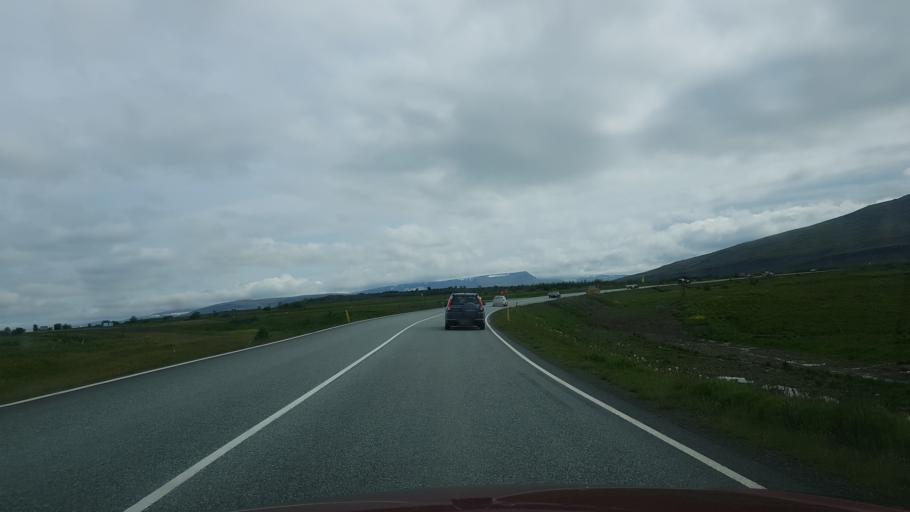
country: IS
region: West
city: Borgarnes
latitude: 64.3888
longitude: -21.8473
